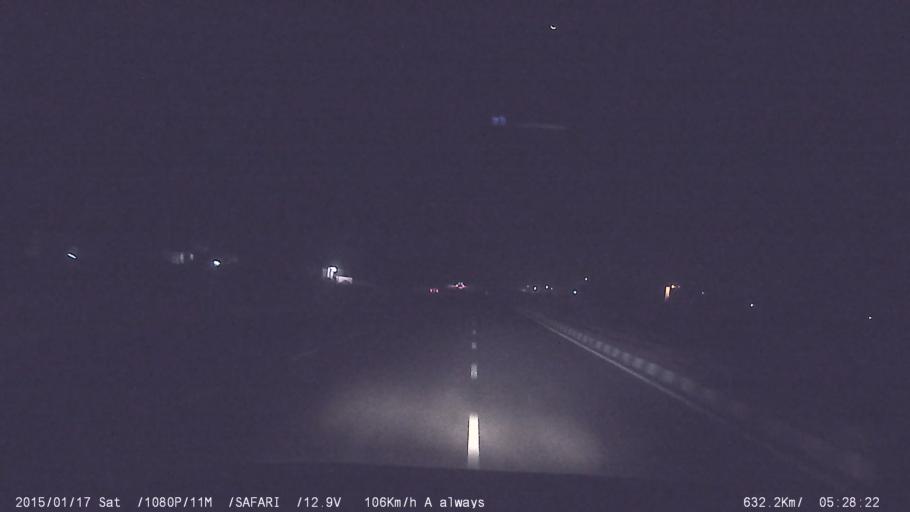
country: IN
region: Tamil Nadu
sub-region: Vellore
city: Arcot
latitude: 12.9258
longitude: 79.2712
